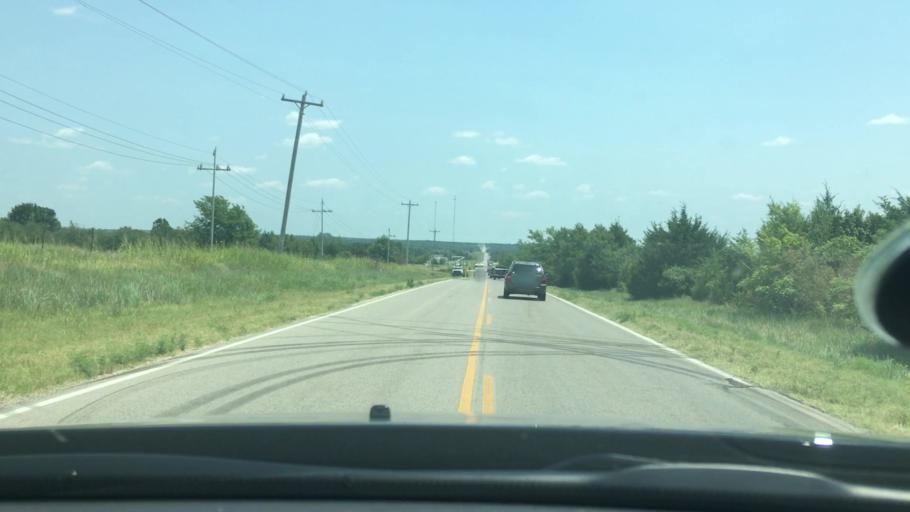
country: US
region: Oklahoma
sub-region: Garvin County
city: Stratford
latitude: 34.7967
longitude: -96.9057
